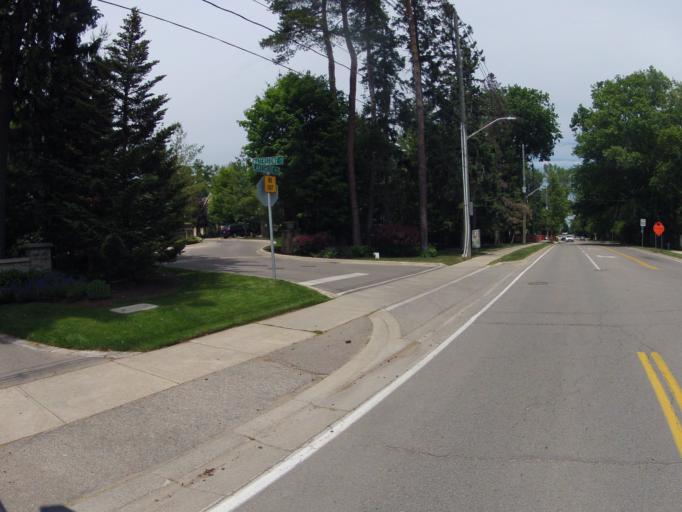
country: CA
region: Ontario
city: Oakville
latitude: 43.4564
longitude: -79.6569
